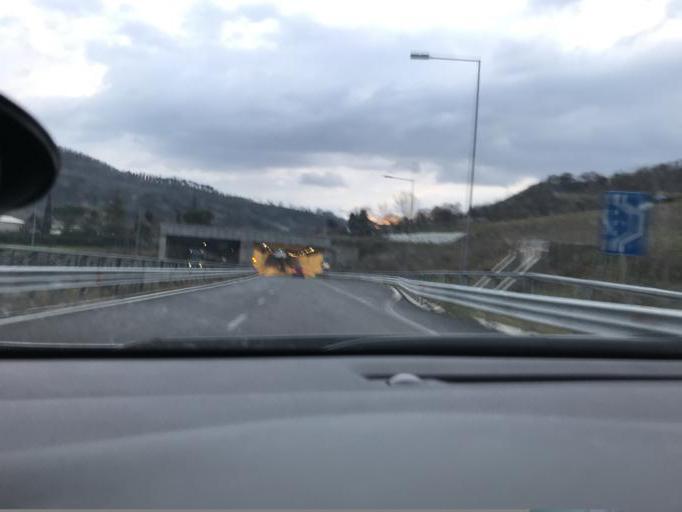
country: IT
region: Umbria
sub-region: Provincia di Perugia
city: Valfabbrica
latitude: 43.1466
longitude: 12.5657
